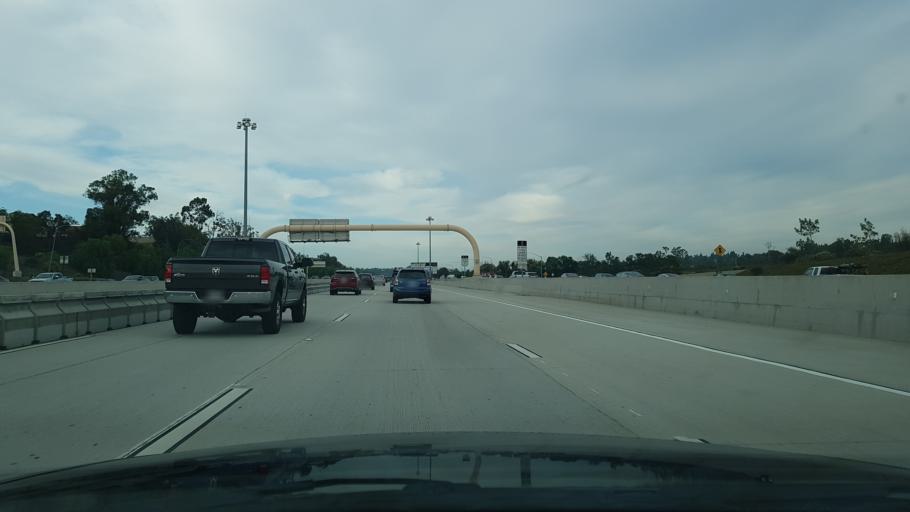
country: US
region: California
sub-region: San Diego County
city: Poway
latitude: 32.9652
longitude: -117.0949
